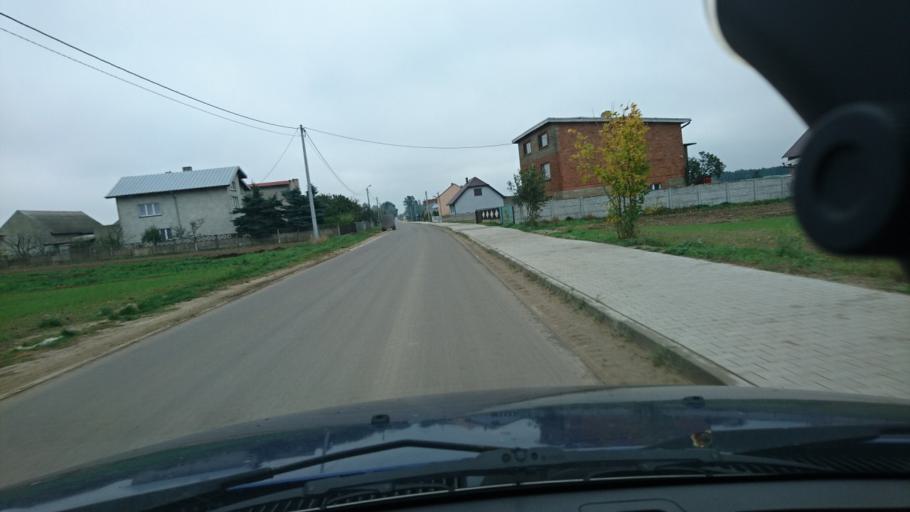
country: PL
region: Greater Poland Voivodeship
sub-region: Powiat ostrowski
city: Odolanow
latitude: 51.5738
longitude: 17.6152
